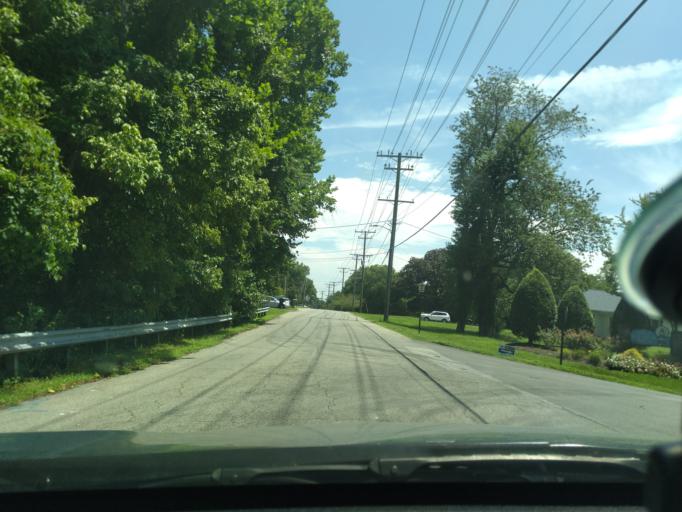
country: US
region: Maryland
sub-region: Calvert County
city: Chesapeake Beach
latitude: 38.6965
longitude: -76.5470
